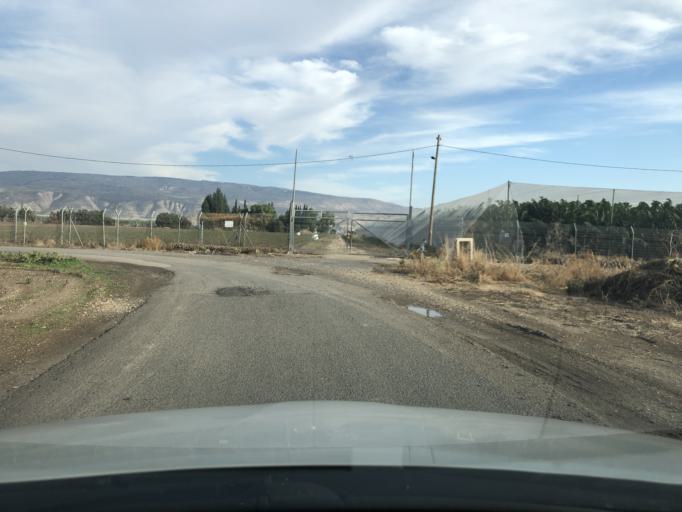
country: IL
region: Northern District
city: Yavne'el
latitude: 32.6562
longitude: 35.5837
